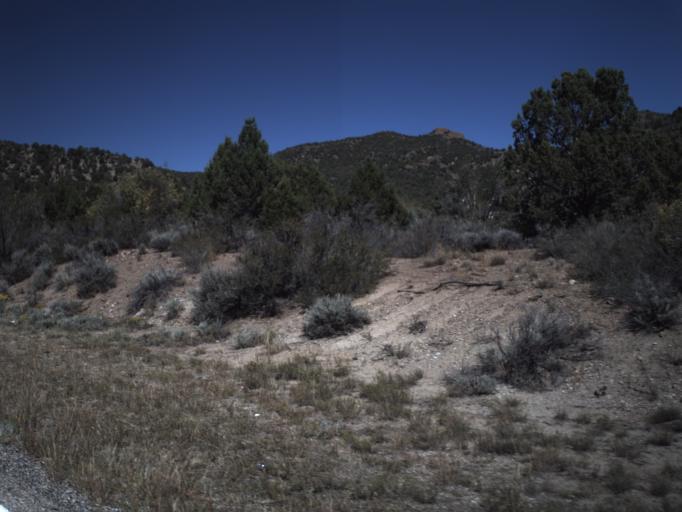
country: US
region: Utah
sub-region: Washington County
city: Enterprise
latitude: 37.4530
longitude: -113.6220
